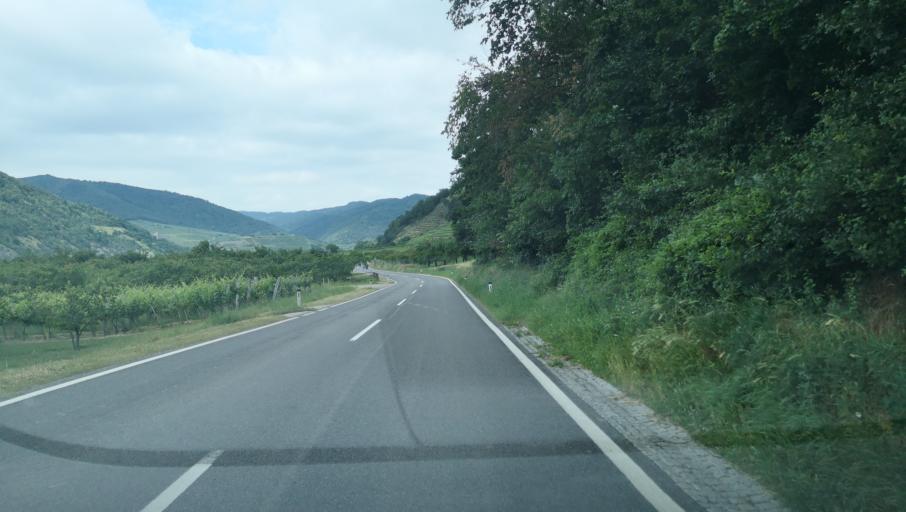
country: AT
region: Lower Austria
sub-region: Politischer Bezirk Krems
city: Spitz
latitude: 48.3390
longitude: 15.4107
